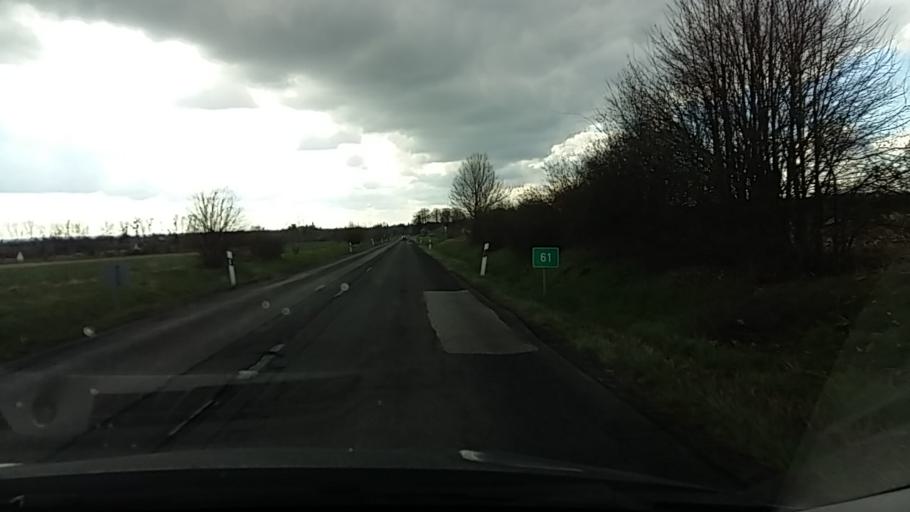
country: HU
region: Somogy
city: Bohonye
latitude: 46.4262
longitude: 17.3800
